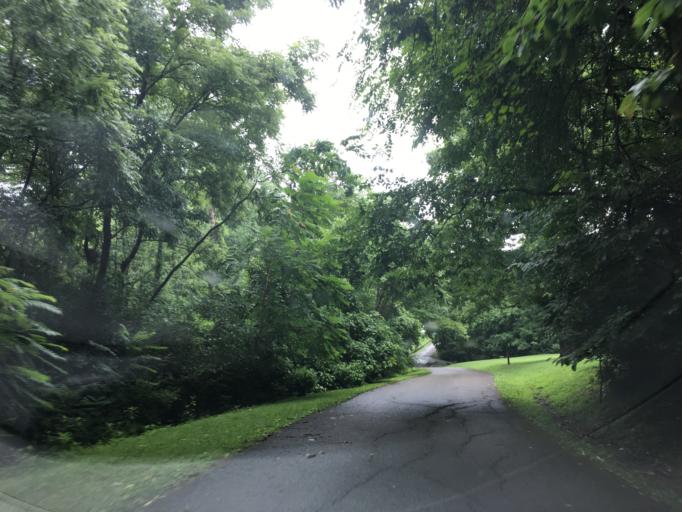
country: US
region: Tennessee
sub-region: Davidson County
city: Belle Meade
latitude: 36.0608
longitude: -86.8970
